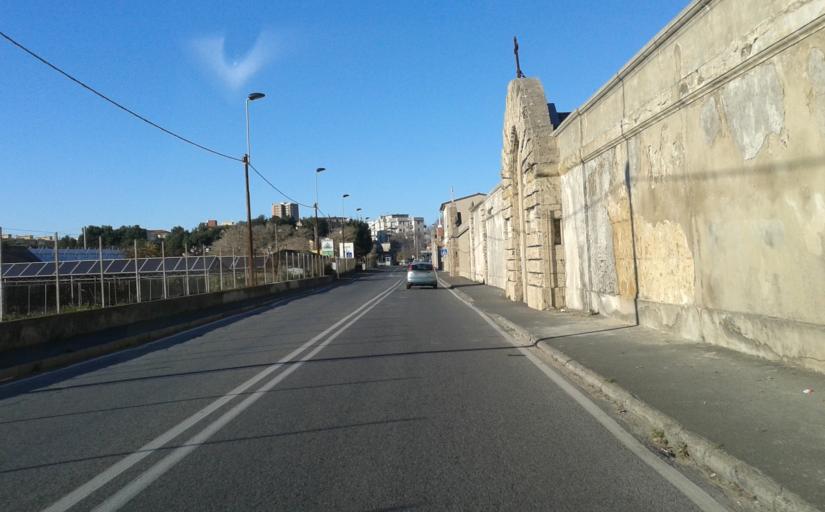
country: IT
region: Tuscany
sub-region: Provincia di Livorno
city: Livorno
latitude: 43.5301
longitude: 10.3208
